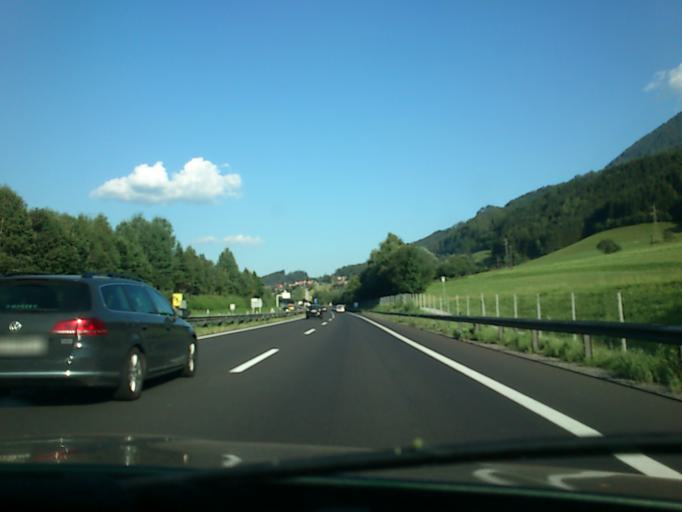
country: AT
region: Styria
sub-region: Politischer Bezirk Liezen
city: Rottenmann
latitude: 47.5249
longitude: 14.3377
